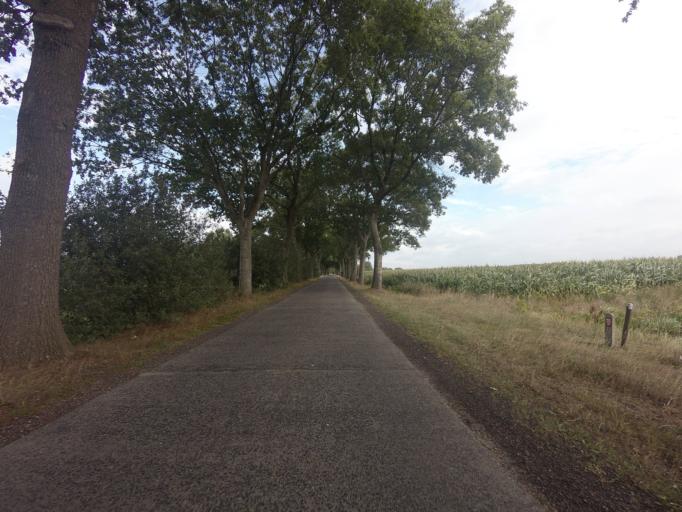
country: NL
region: Friesland
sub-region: Gemeente Heerenveen
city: Jubbega
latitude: 52.9735
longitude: 6.1504
